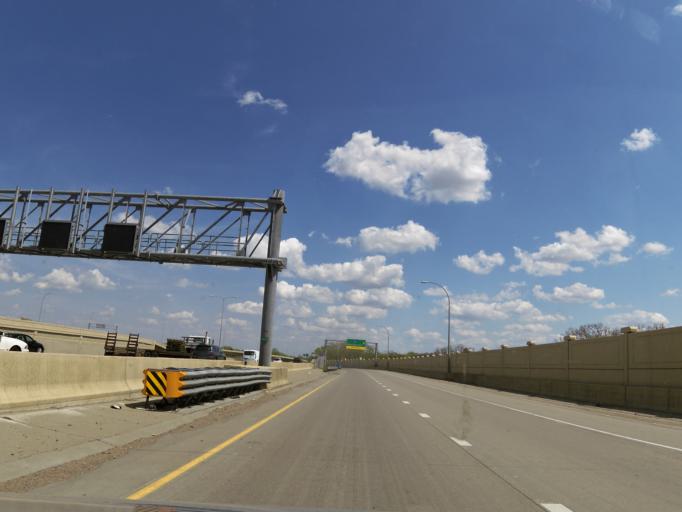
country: US
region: Minnesota
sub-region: Hennepin County
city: Richfield
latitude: 44.8899
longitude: -93.2806
